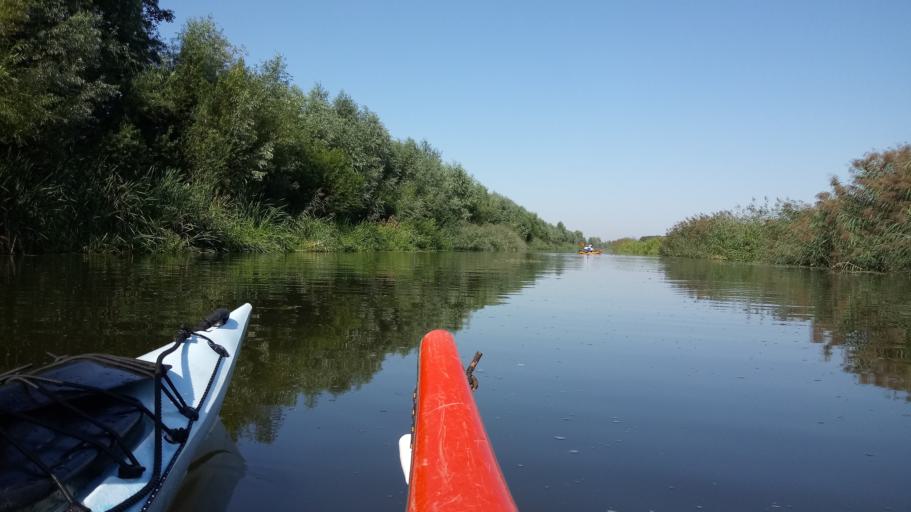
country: NL
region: Gelderland
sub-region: Berkelland
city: Eibergen
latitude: 52.0962
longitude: 6.7121
